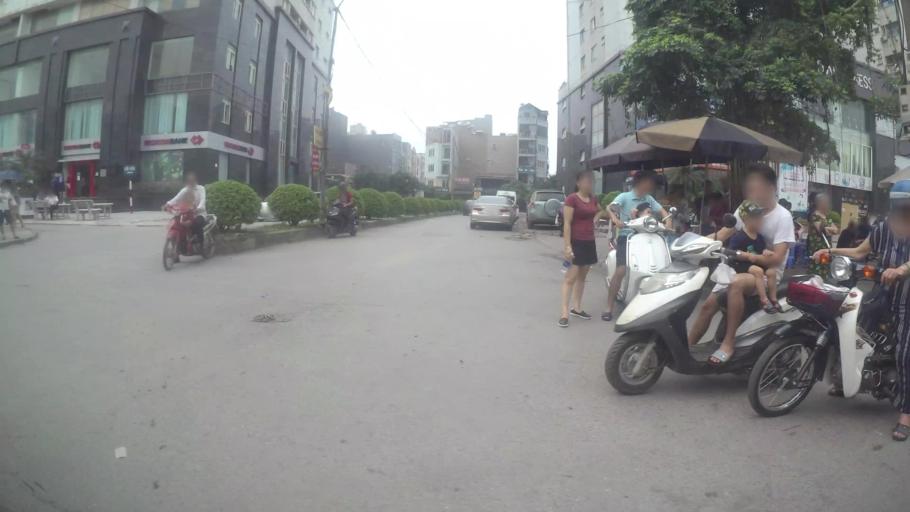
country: VN
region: Ha Noi
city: Ha Dong
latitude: 20.9689
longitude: 105.7686
